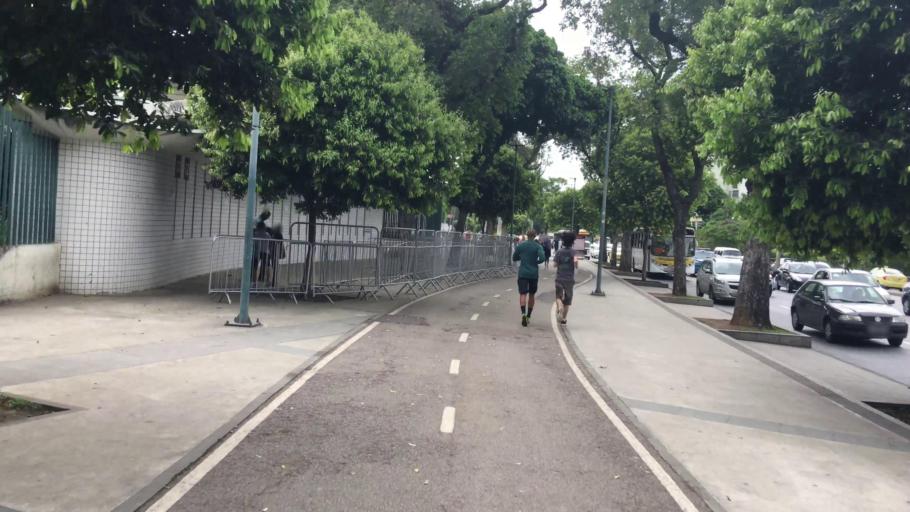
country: BR
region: Rio de Janeiro
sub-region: Rio De Janeiro
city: Rio de Janeiro
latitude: -22.9146
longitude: -43.2289
